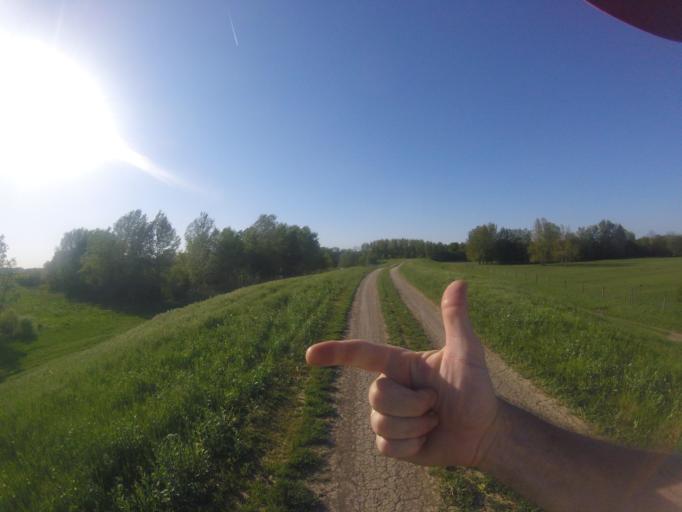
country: HU
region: Bekes
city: Gyula
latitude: 46.7046
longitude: 21.3062
